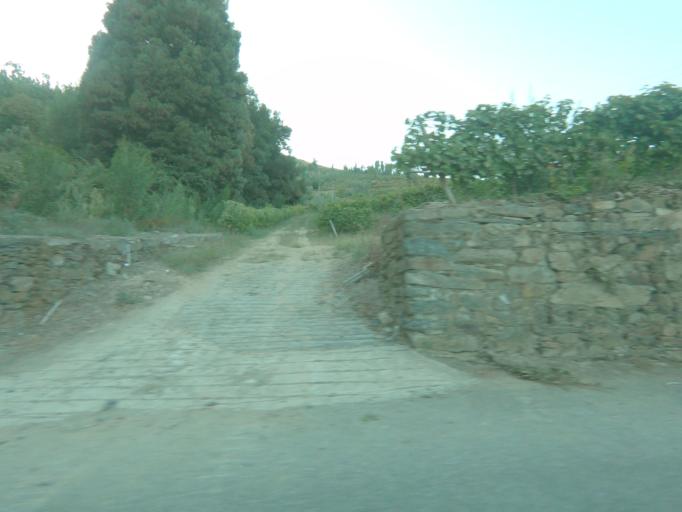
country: PT
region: Vila Real
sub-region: Mesao Frio
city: Mesao Frio
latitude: 41.1966
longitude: -7.8615
